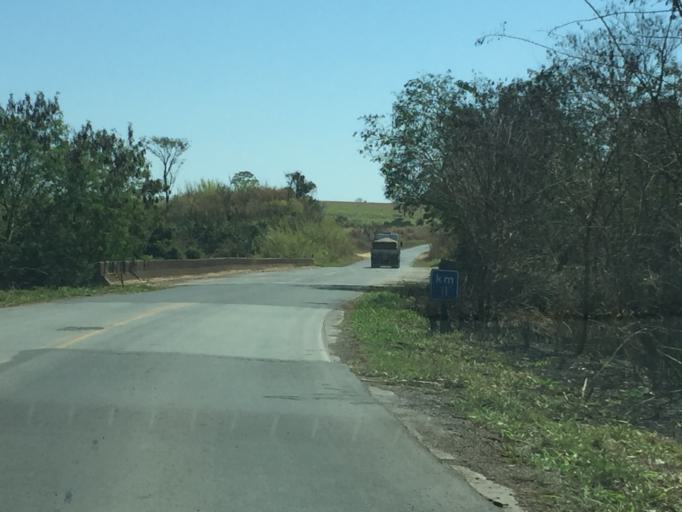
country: BR
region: Sao Paulo
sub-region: Moji-Guacu
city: Mogi-Gaucu
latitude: -22.3770
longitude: -46.8733
